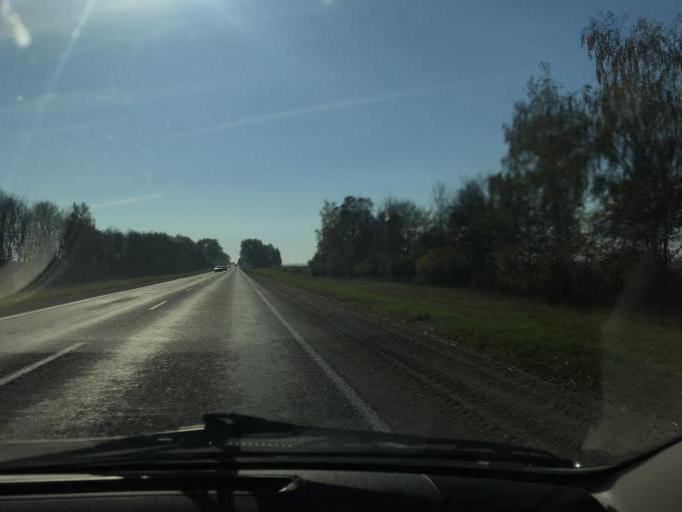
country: BY
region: Minsk
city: Salihorsk
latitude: 52.8445
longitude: 27.4663
